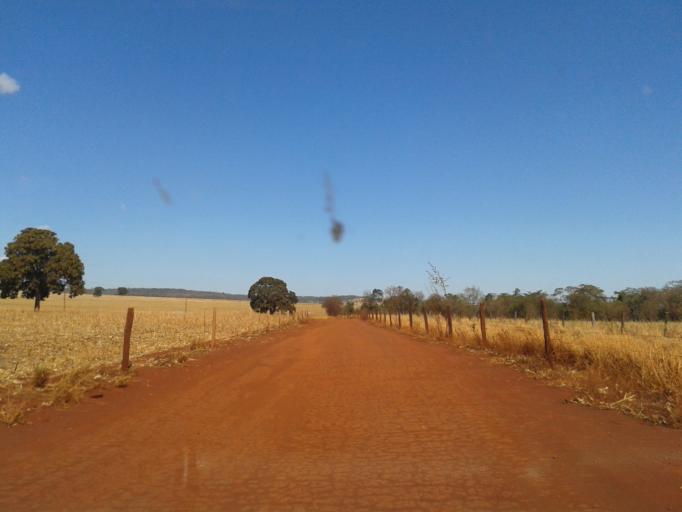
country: BR
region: Minas Gerais
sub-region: Centralina
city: Centralina
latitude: -18.5862
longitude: -49.1466
